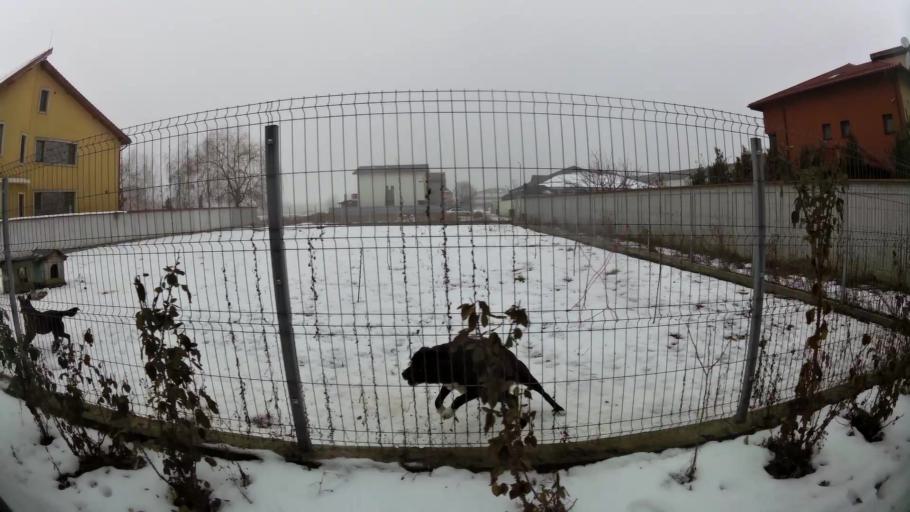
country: RO
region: Ilfov
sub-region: Comuna Chiajna
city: Rosu
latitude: 44.4428
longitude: 25.9996
